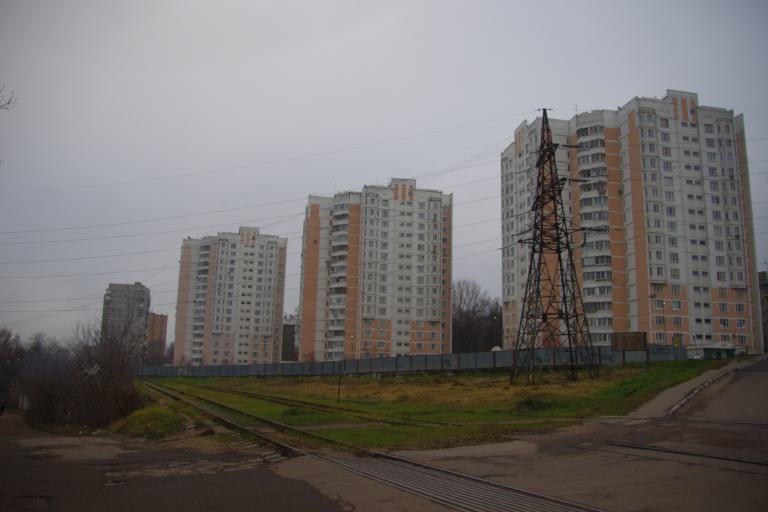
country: RU
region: Moskovskaya
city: Pavshino
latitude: 55.8246
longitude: 37.3427
